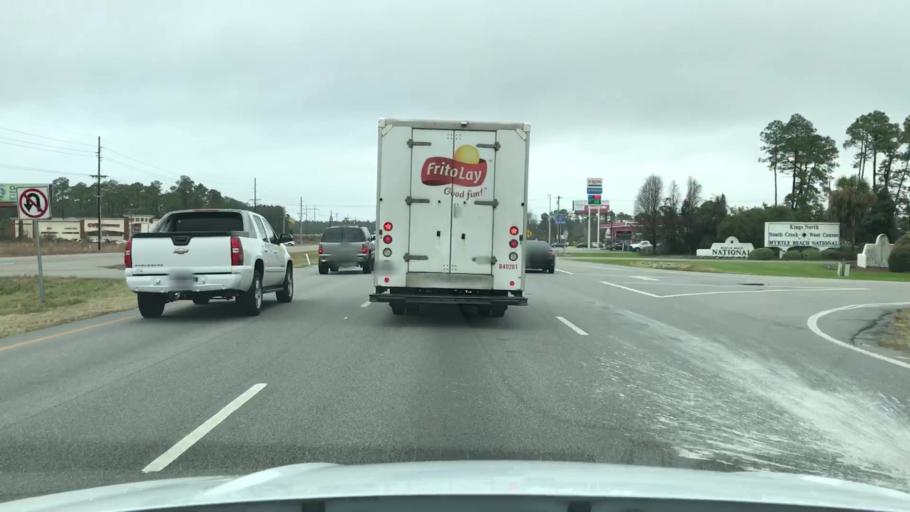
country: US
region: South Carolina
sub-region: Horry County
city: Forestbrook
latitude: 33.7739
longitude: -78.9815
